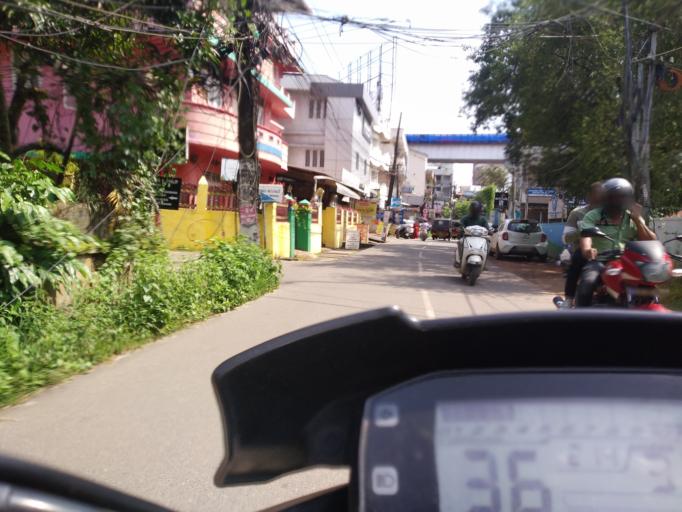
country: IN
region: Kerala
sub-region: Ernakulam
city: Cochin
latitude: 9.9663
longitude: 76.2927
